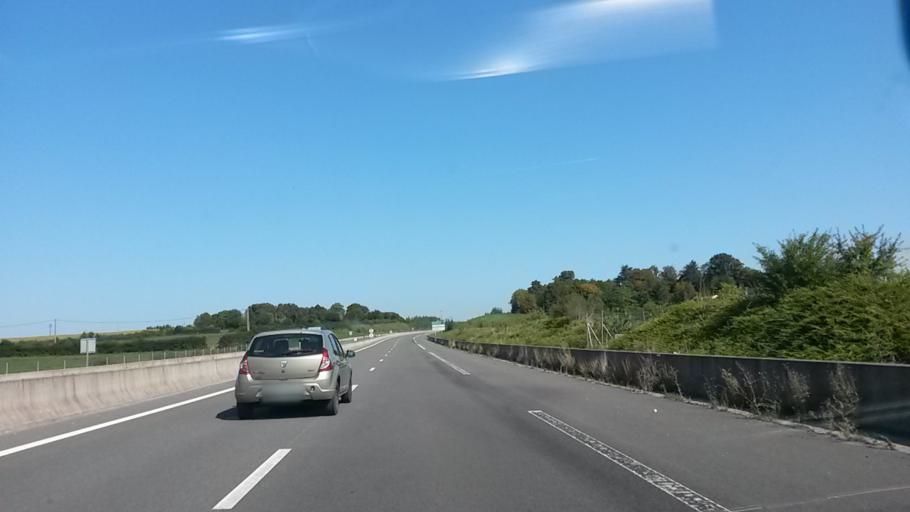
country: FR
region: Nord-Pas-de-Calais
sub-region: Departement du Nord
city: Hautmont
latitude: 50.2122
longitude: 3.9537
